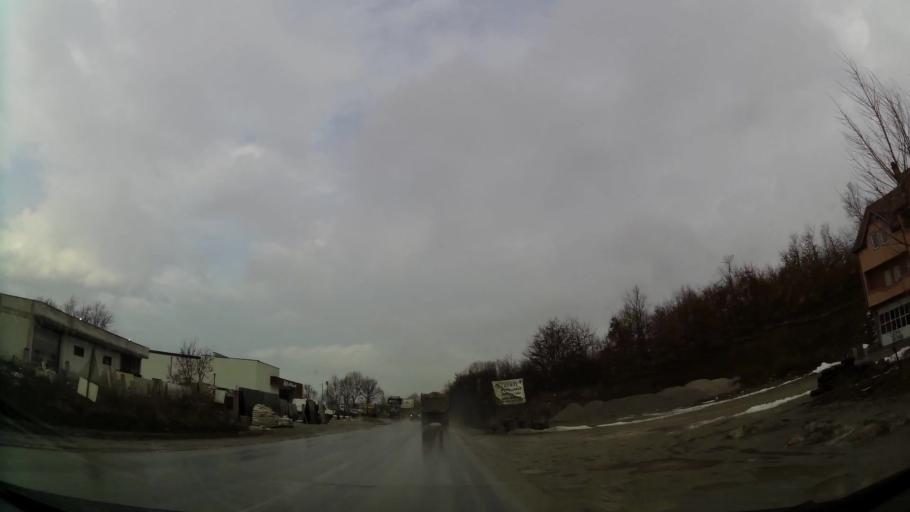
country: XK
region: Ferizaj
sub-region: Komuna e Kacanikut
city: Kacanik
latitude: 42.2502
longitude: 21.2372
